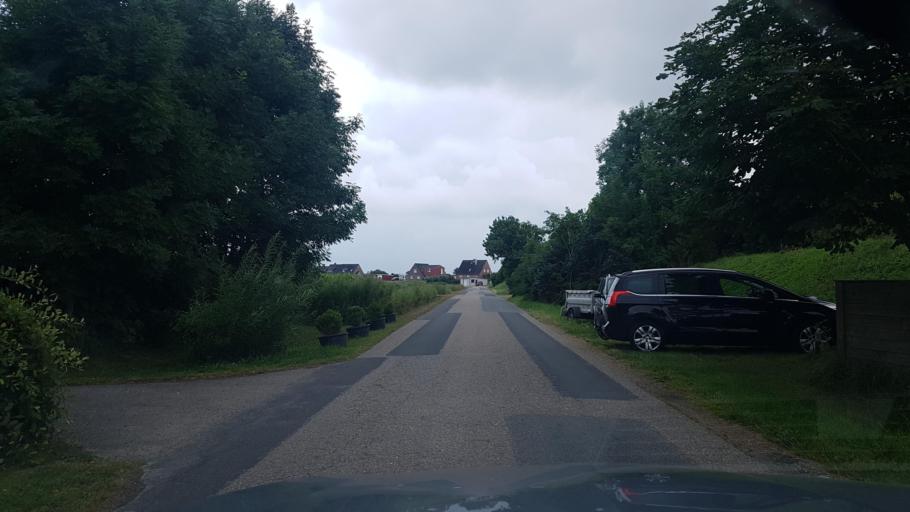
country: DE
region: Schleswig-Holstein
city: Elisabeth-Sophien-Koog
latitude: 54.4840
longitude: 8.8250
